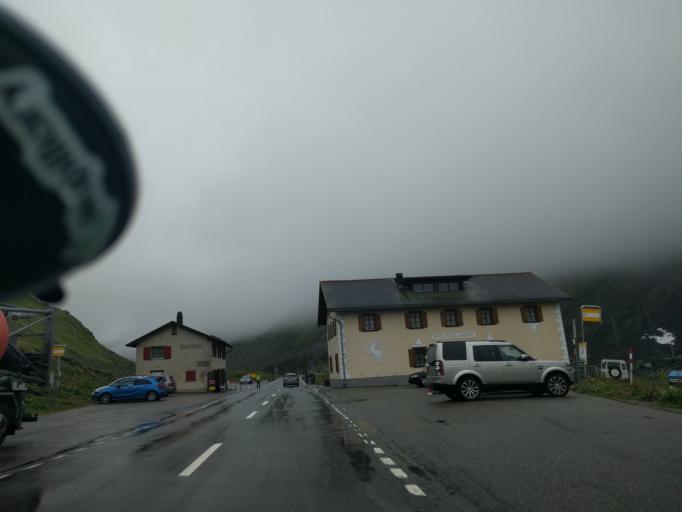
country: CH
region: Grisons
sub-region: Praettigau/Davos District
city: Davos
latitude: 46.7508
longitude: 9.9470
